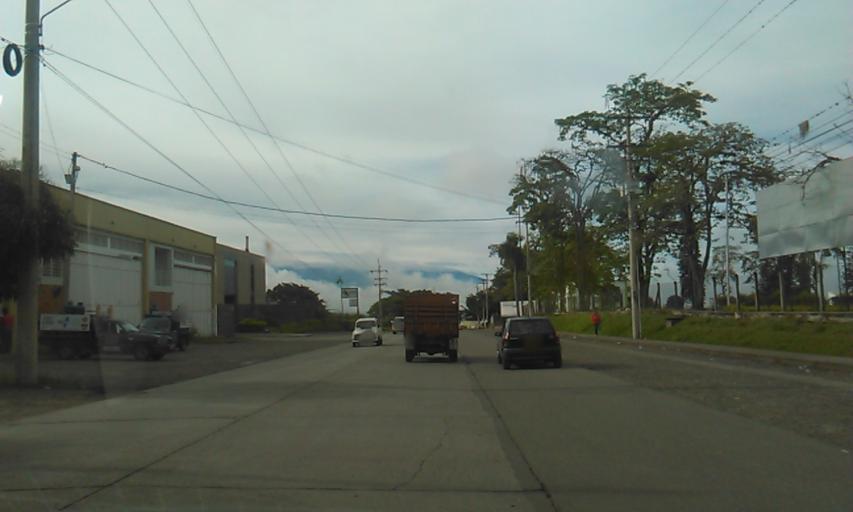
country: CO
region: Quindio
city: Armenia
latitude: 4.5080
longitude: -75.6907
